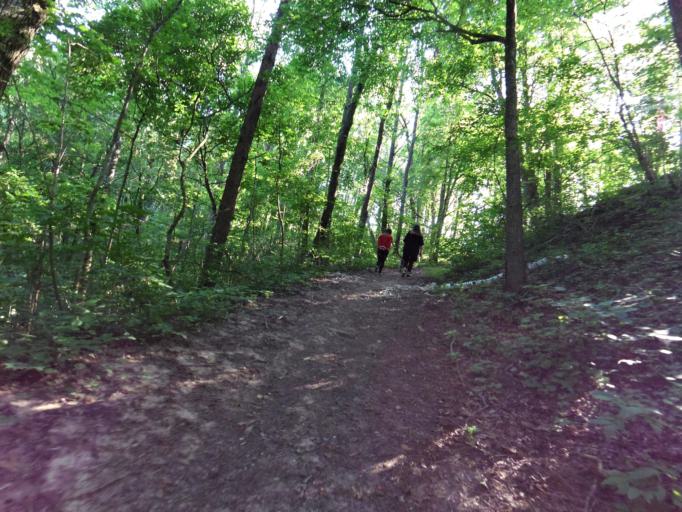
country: LT
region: Vilnius County
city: Lazdynai
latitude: 54.6891
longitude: 25.2198
